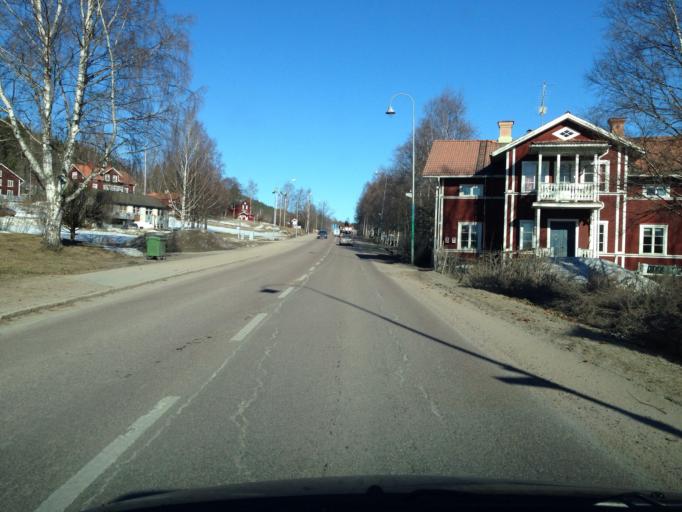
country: SE
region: Gaevleborg
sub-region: Ljusdals Kommun
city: Jaervsoe
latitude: 61.7188
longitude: 16.1700
